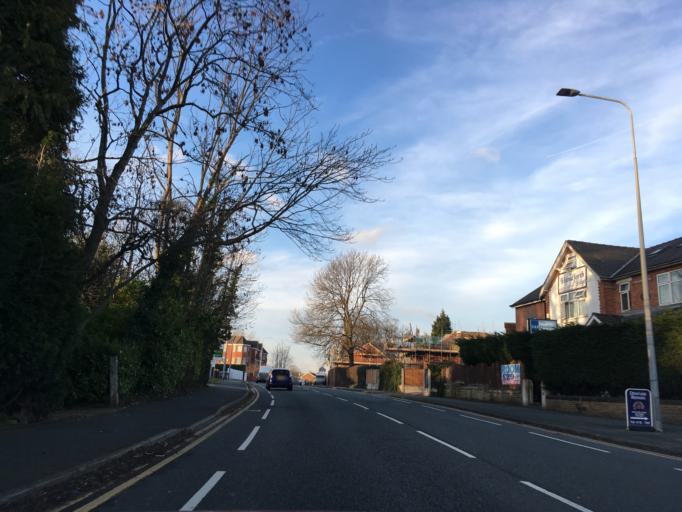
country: GB
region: England
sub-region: Cheshire East
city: Wilmslow
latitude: 53.3544
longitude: -2.2172
